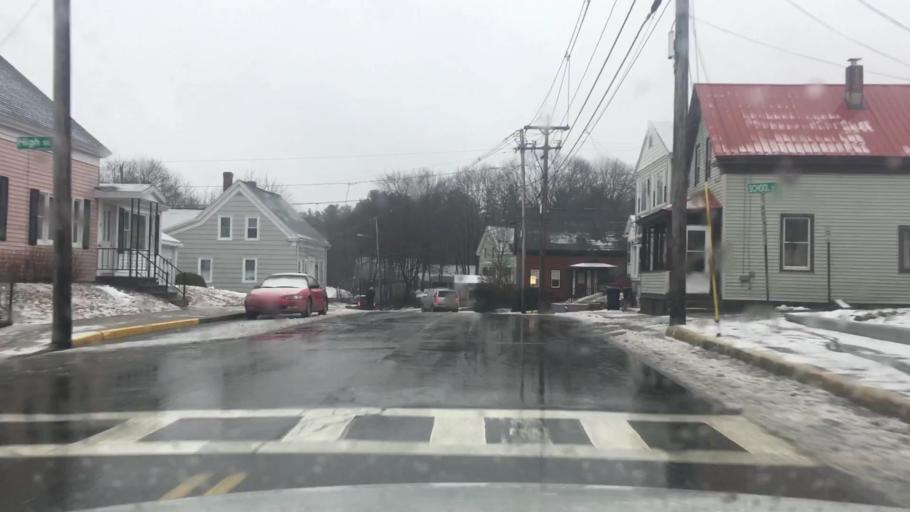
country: US
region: Maine
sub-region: York County
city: Biddeford
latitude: 43.4889
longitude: -70.4514
